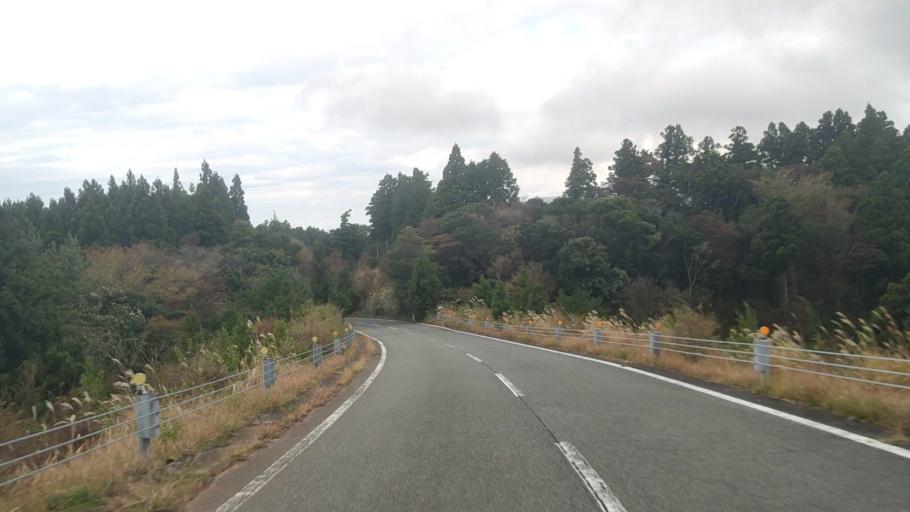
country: JP
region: Shizuoka
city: Heda
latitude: 34.8995
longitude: 138.8458
